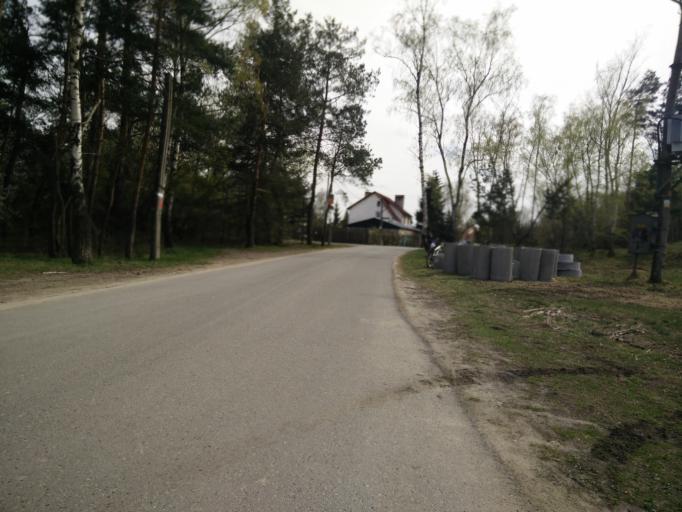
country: PL
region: Masovian Voivodeship
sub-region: Powiat warszawski zachodni
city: Izabelin
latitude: 52.2910
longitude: 20.8393
